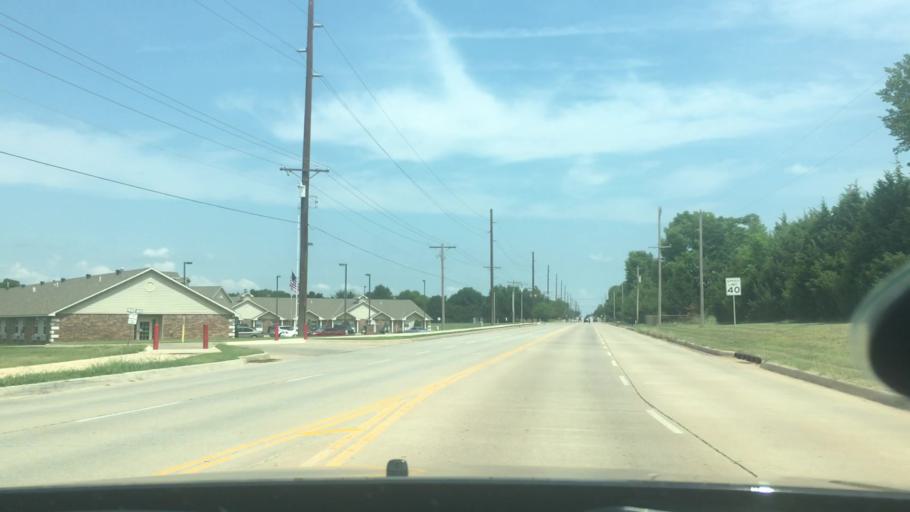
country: US
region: Oklahoma
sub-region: Pottawatomie County
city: Shawnee
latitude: 35.3481
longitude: -96.8942
